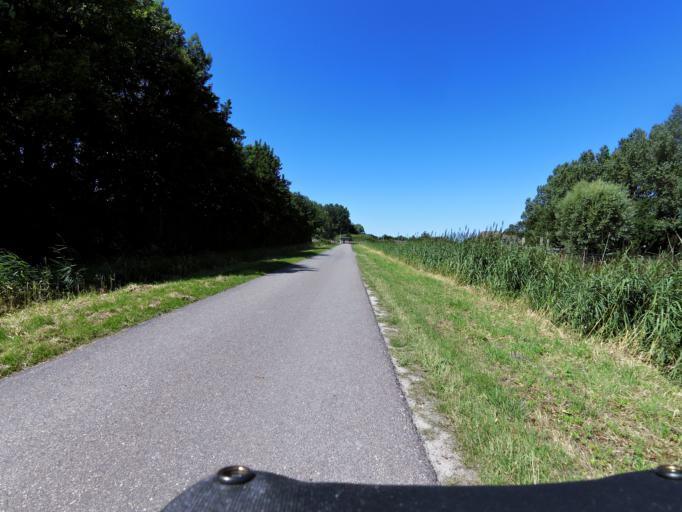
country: NL
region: South Holland
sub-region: Gemeente Goeree-Overflakkee
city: Ouddorp
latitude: 51.8168
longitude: 3.9517
